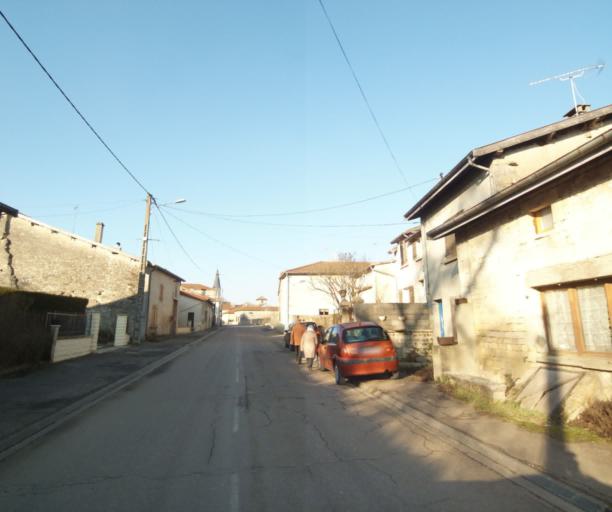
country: FR
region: Champagne-Ardenne
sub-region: Departement de la Haute-Marne
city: Bienville
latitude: 48.5811
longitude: 5.0885
